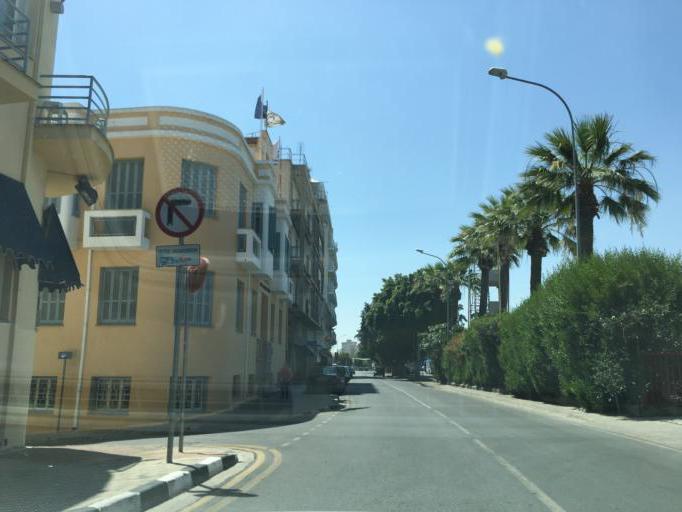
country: CY
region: Lefkosia
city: Nicosia
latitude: 35.1727
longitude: 33.3576
